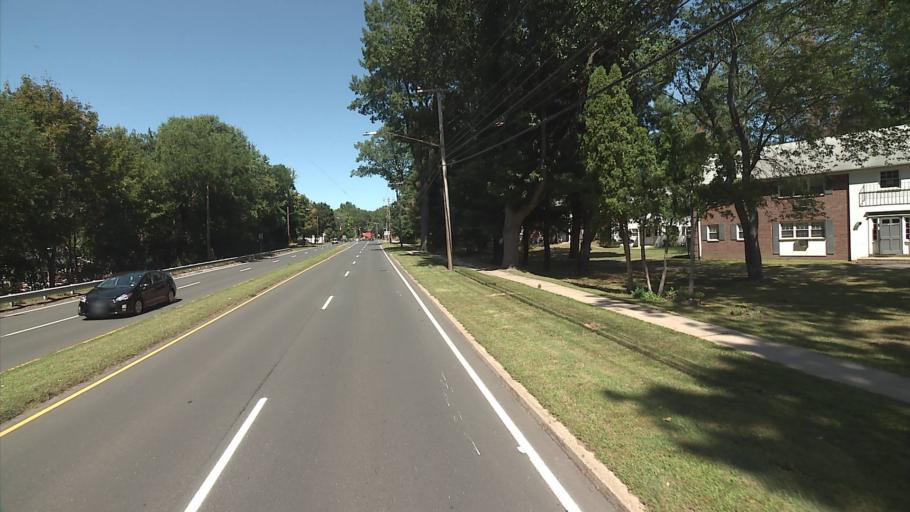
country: US
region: Connecticut
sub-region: Hartford County
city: Windsor
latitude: 41.8274
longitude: -72.6560
